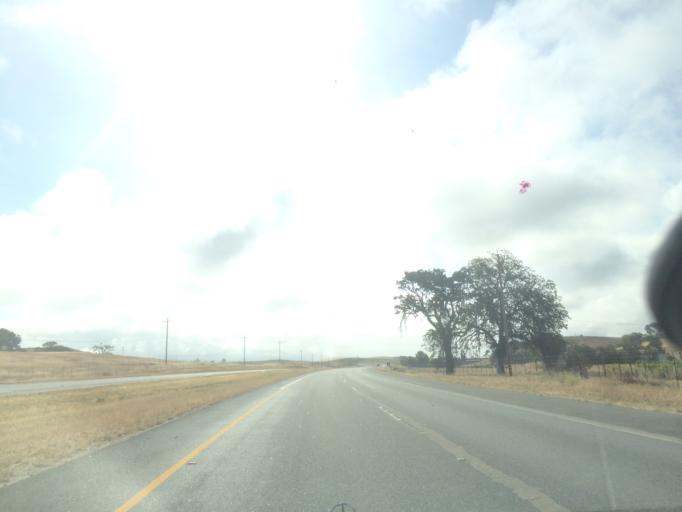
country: US
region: California
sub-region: San Luis Obispo County
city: Paso Robles
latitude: 35.6589
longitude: -120.5451
